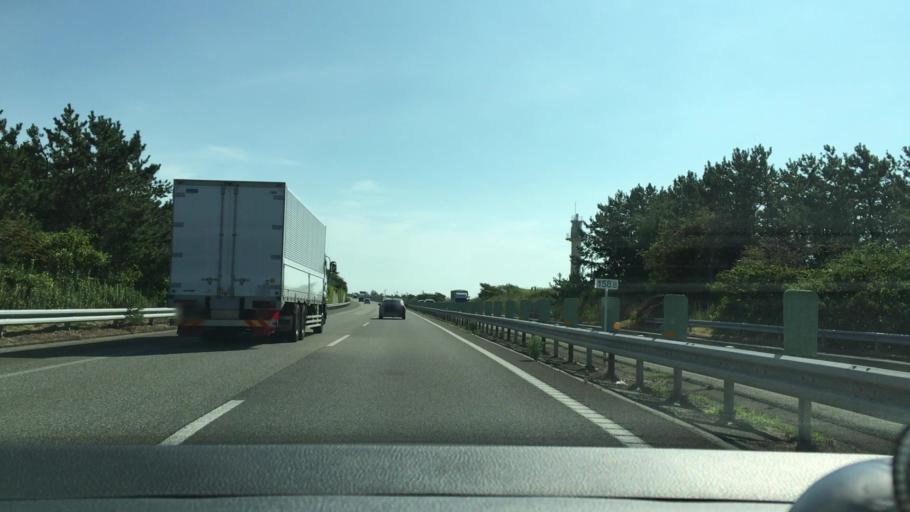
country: JP
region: Ishikawa
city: Matsuto
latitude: 36.4941
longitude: 136.4859
